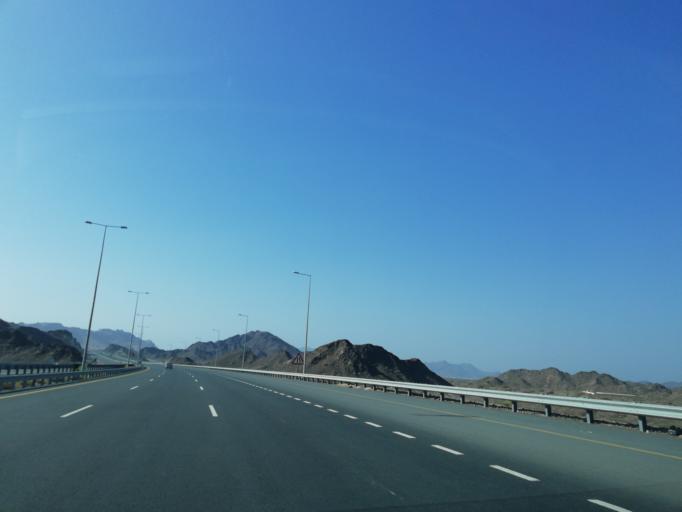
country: OM
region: Muhafazat ad Dakhiliyah
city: Sufalat Sama'il
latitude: 22.9794
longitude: 58.2336
